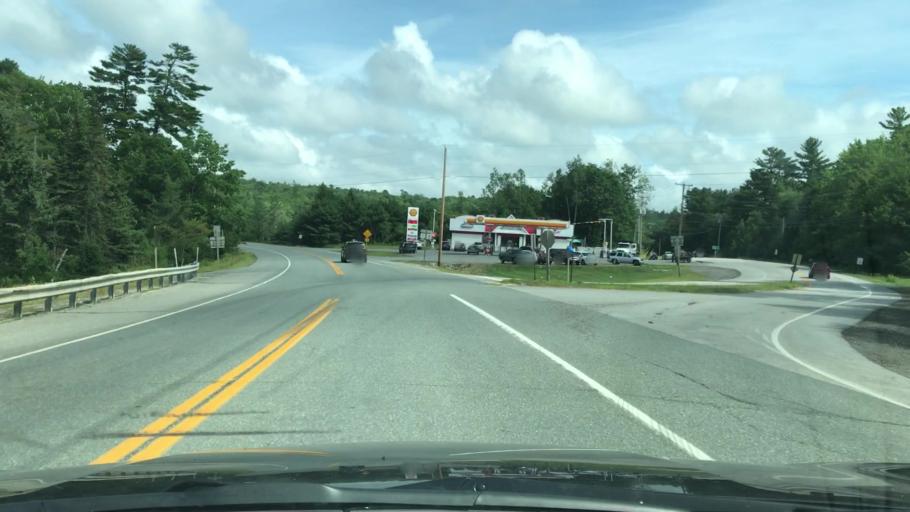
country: US
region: Maine
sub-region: Hancock County
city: Orland
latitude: 44.5603
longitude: -68.7096
